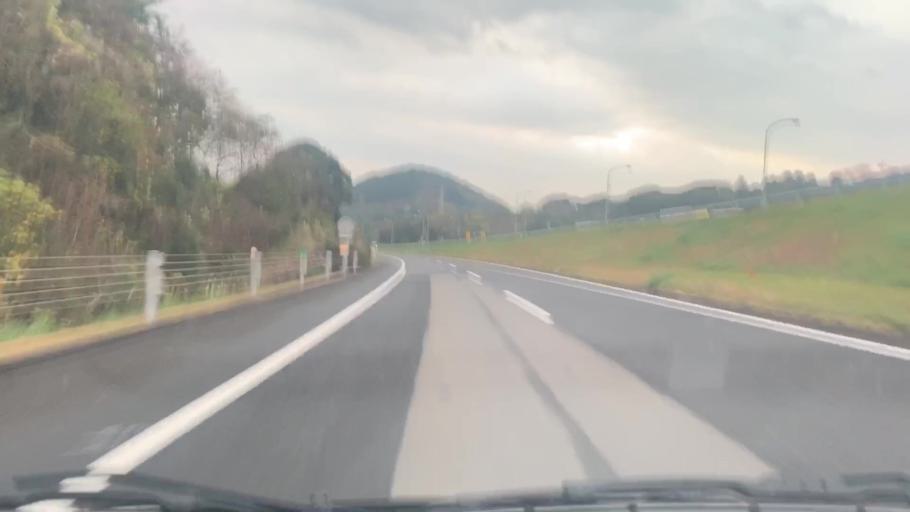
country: JP
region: Nagasaki
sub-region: Isahaya-shi
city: Isahaya
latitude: 32.8622
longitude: 130.0013
